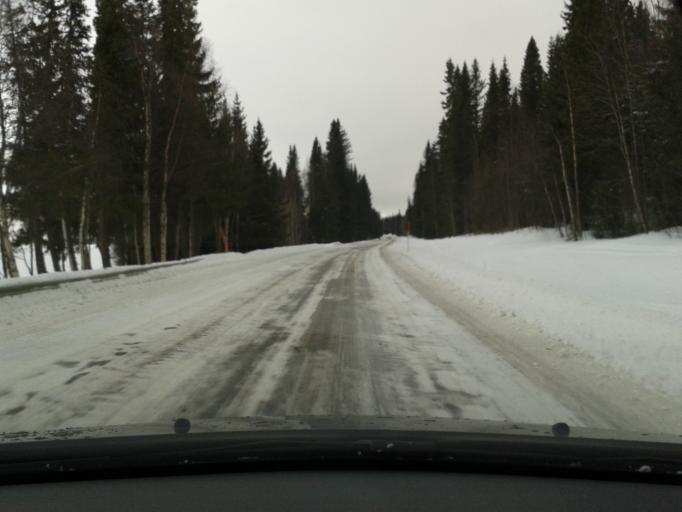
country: SE
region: Vaesterbotten
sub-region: Vilhelmina Kommun
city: Sjoberg
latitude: 64.6636
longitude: 16.3083
